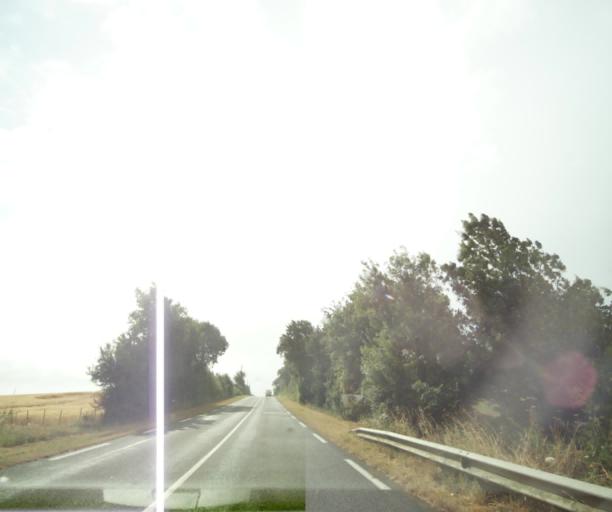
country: FR
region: Pays de la Loire
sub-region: Departement de la Vendee
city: Moutiers-les-Mauxfaits
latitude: 46.4561
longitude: -1.4283
